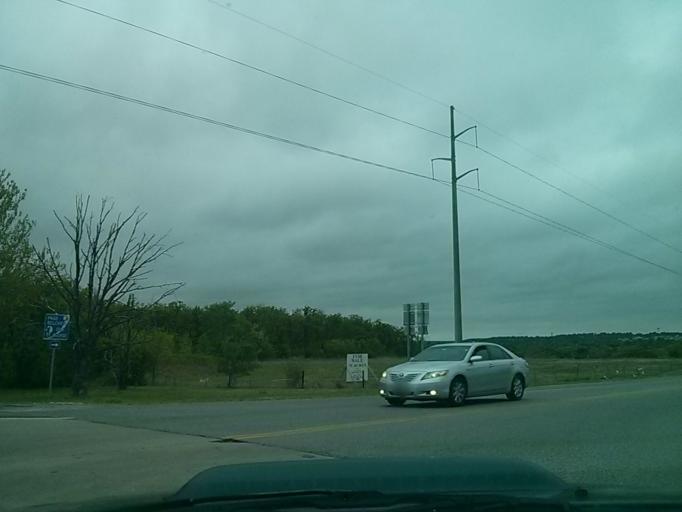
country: US
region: Oklahoma
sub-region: Tulsa County
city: Oakhurst
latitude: 36.0754
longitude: -96.0074
